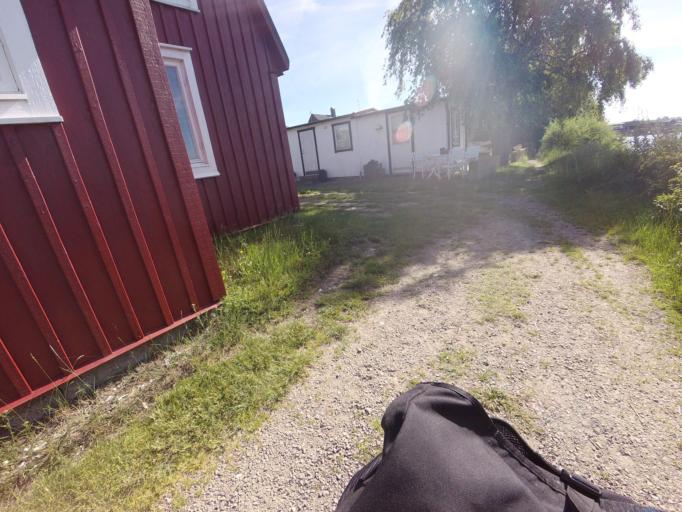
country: SE
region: Skane
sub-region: Trelleborgs Kommun
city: Skare
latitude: 55.3759
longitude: 13.0506
